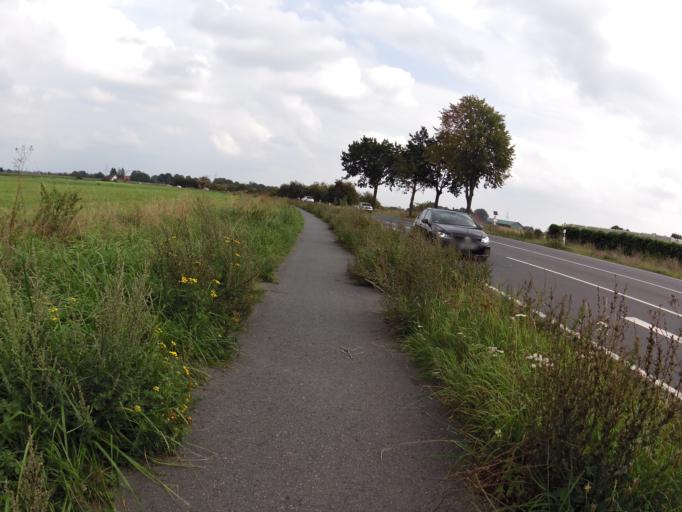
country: DE
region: Lower Saxony
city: Blender
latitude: 52.9252
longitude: 9.1788
